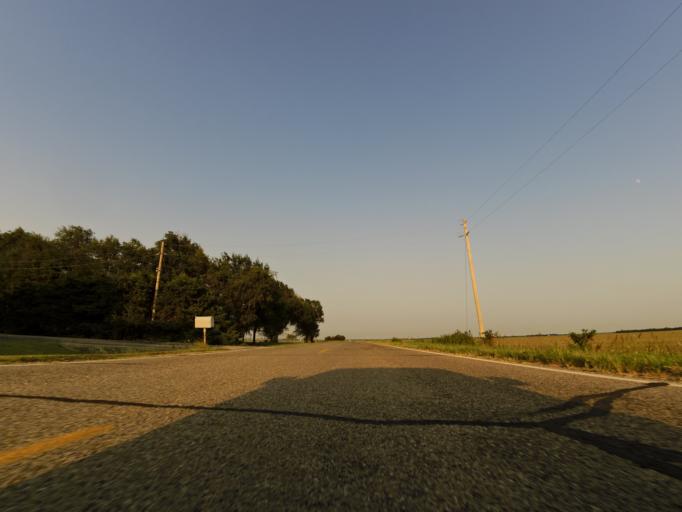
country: US
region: Kansas
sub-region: Reno County
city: South Hutchinson
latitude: 37.9700
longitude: -98.0091
